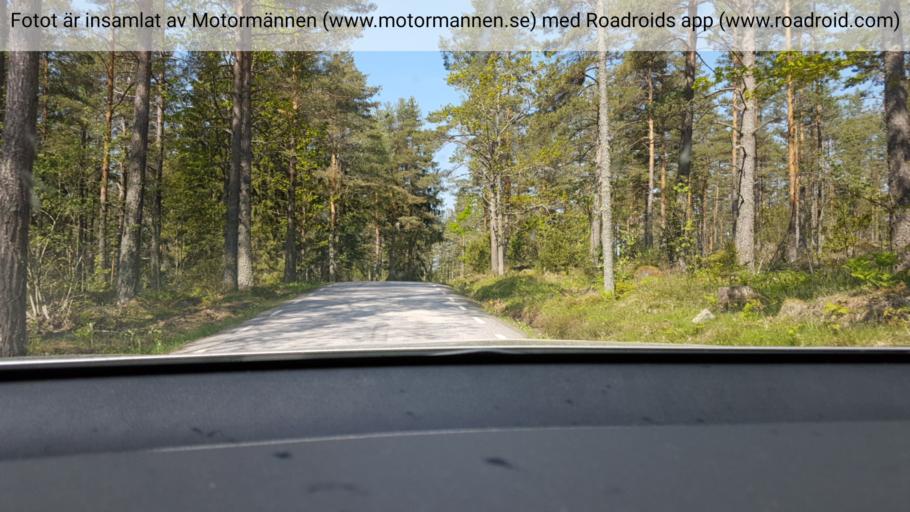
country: SE
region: Kalmar
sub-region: Vasterviks Kommun
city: Gamleby
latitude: 57.8774
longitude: 16.4461
